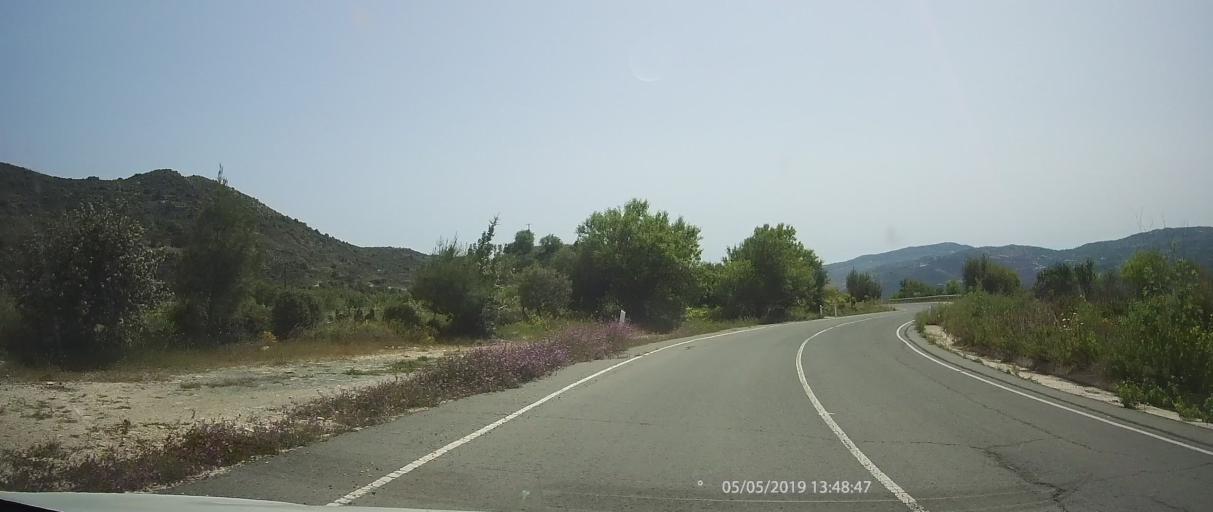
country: CY
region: Limassol
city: Pachna
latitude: 34.8545
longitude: 32.7510
